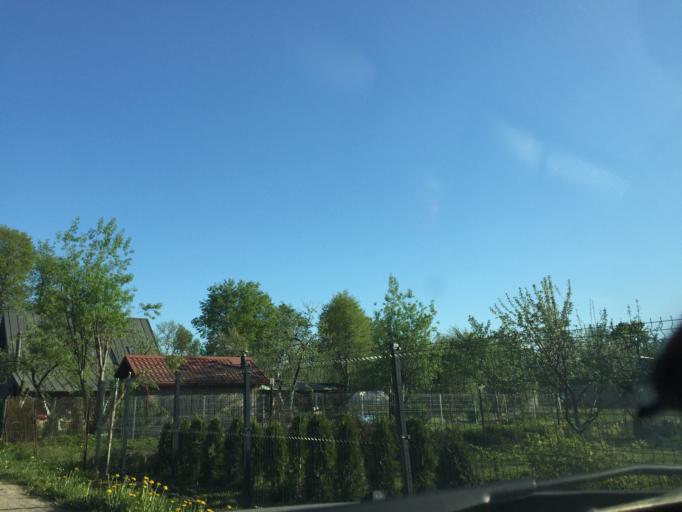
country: LV
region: Sigulda
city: Sigulda
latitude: 57.1478
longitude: 24.8607
